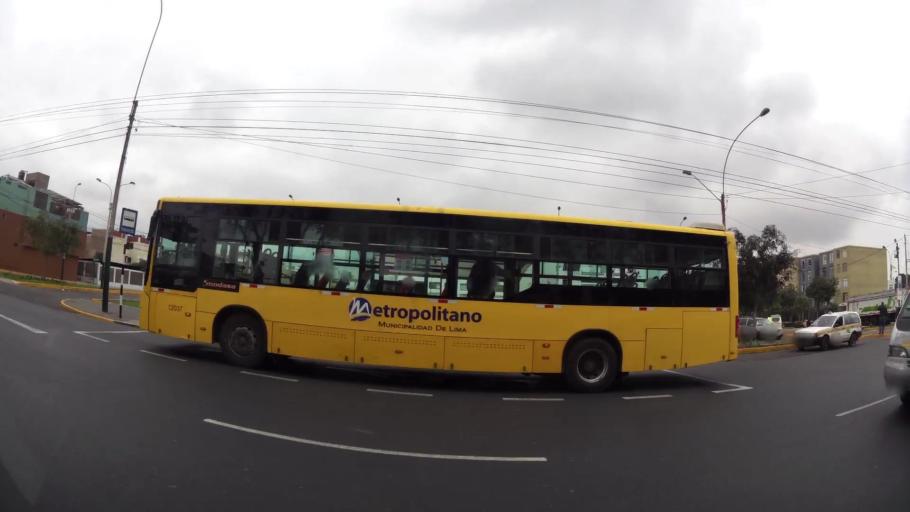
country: PE
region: Lima
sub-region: Lima
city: Surco
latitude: -12.1517
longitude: -76.9888
